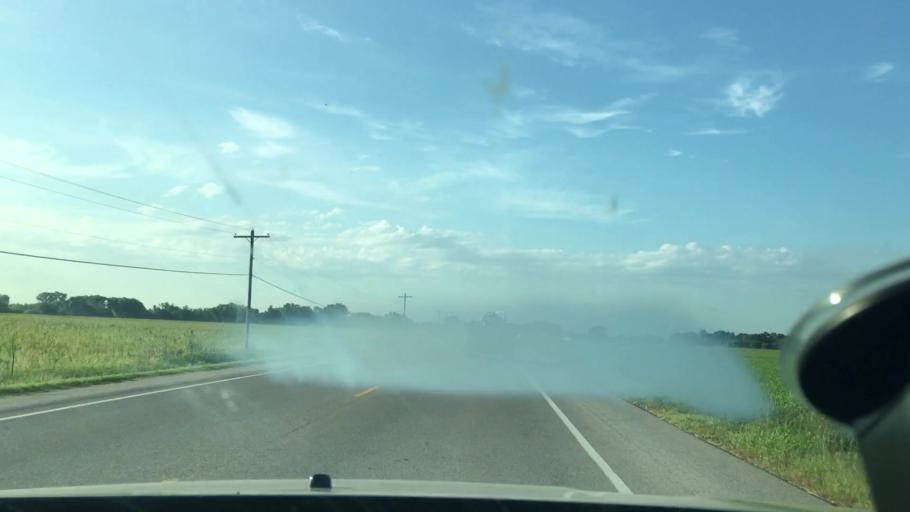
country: US
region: Oklahoma
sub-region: Garvin County
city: Wynnewood
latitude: 34.6584
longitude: -97.2025
